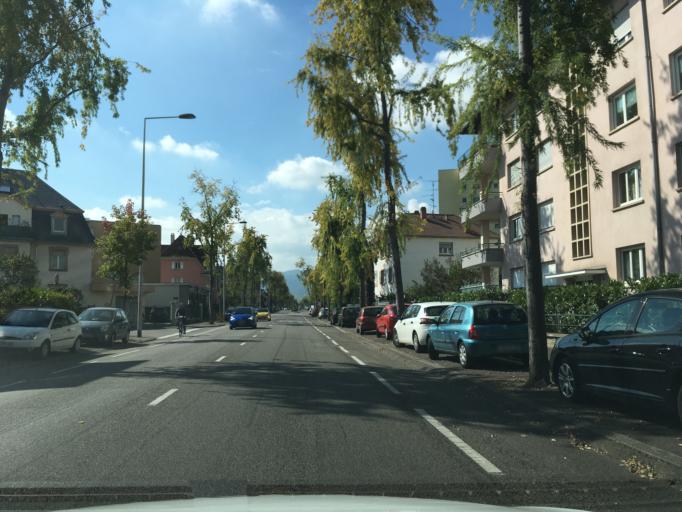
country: FR
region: Alsace
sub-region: Departement du Haut-Rhin
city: Colmar
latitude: 48.0734
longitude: 7.3410
